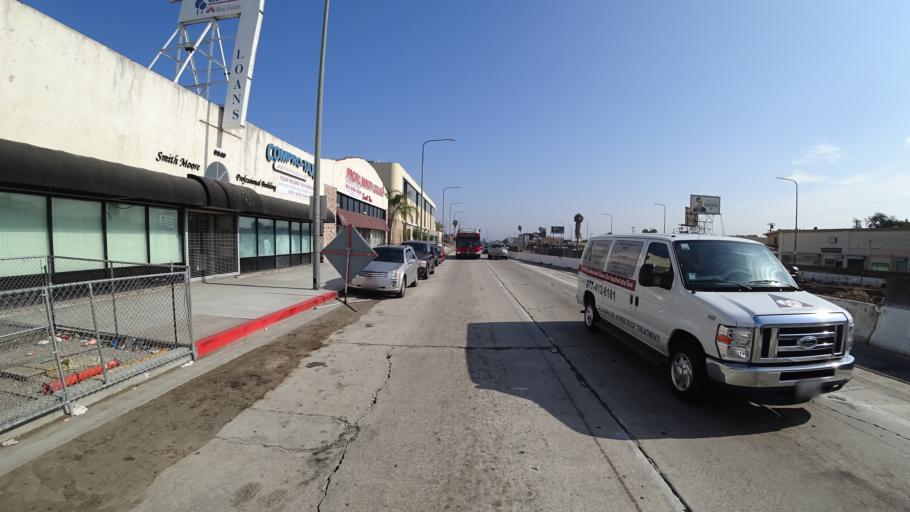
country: US
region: California
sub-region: Los Angeles County
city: View Park-Windsor Hills
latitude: 33.9935
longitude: -118.3311
